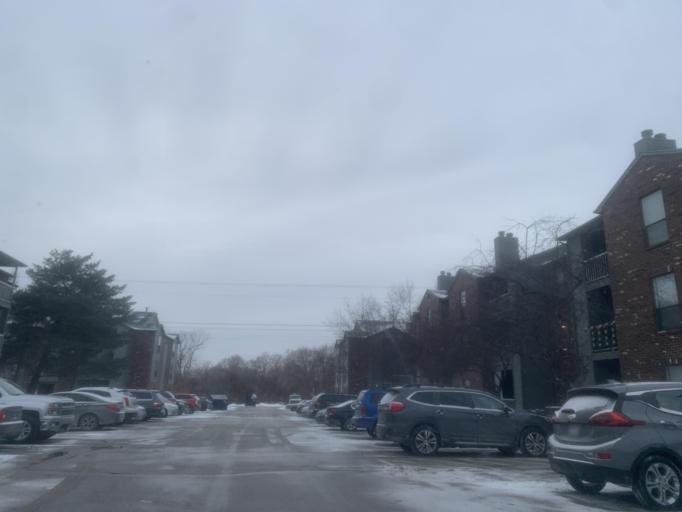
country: US
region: Nebraska
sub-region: Douglas County
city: Ralston
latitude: 41.2711
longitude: -96.0846
